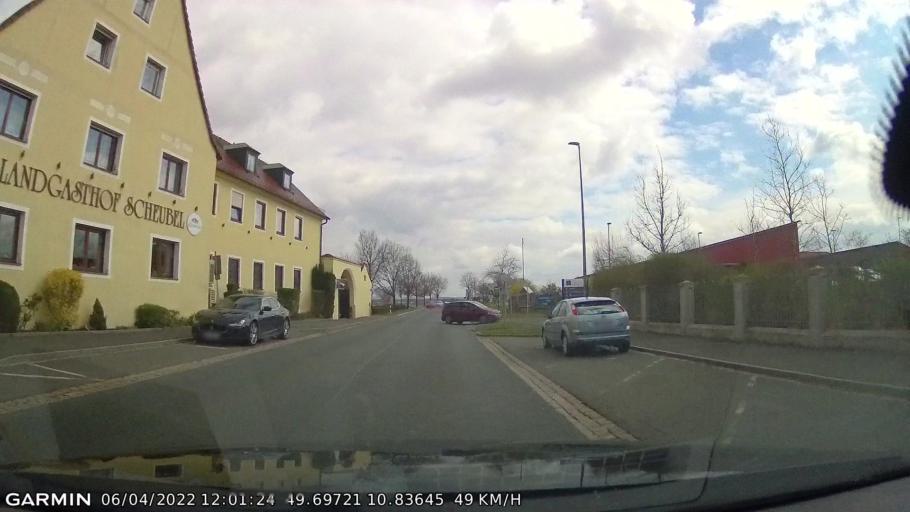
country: DE
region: Bavaria
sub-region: Regierungsbezirk Mittelfranken
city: Gremsdorf
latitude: 49.6973
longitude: 10.8366
